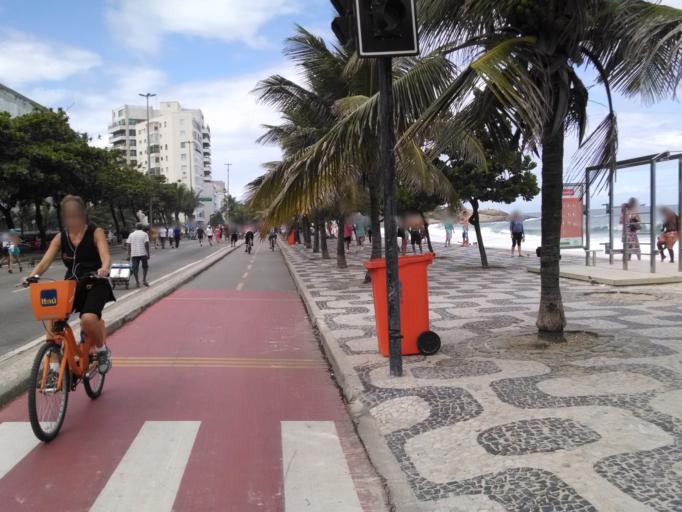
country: BR
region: Rio de Janeiro
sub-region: Rio De Janeiro
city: Rio de Janeiro
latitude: -22.9876
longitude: -43.1961
